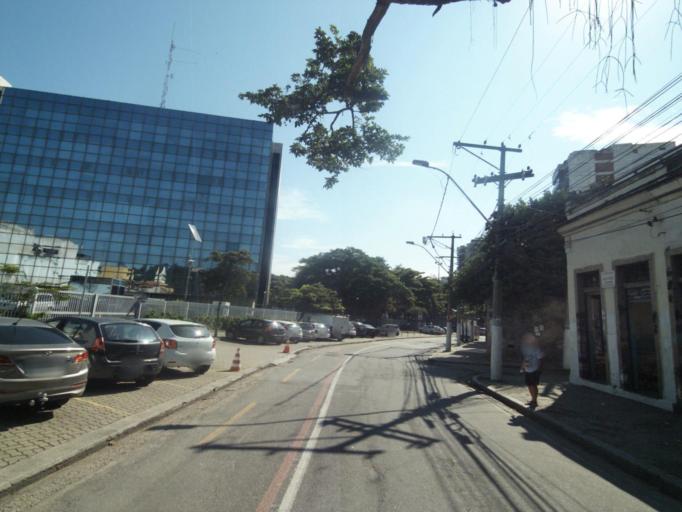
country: BR
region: Rio de Janeiro
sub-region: Niteroi
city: Niteroi
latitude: -22.8989
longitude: -43.1296
